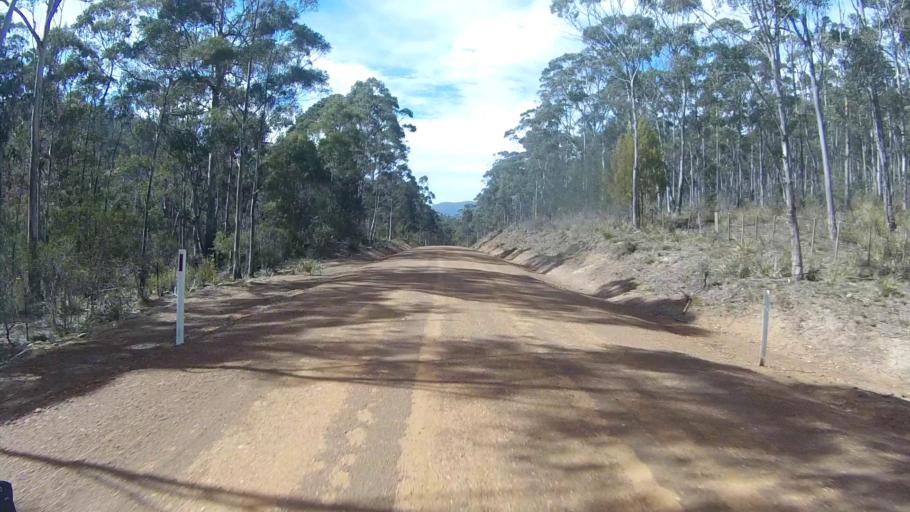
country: AU
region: Tasmania
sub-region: Sorell
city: Sorell
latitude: -42.6186
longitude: 147.9012
